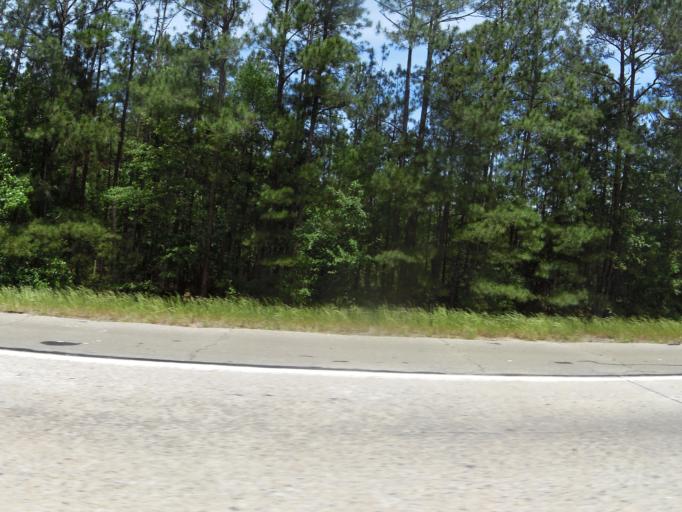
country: US
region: Georgia
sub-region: Bryan County
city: Pembroke
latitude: 32.1985
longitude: -81.4826
